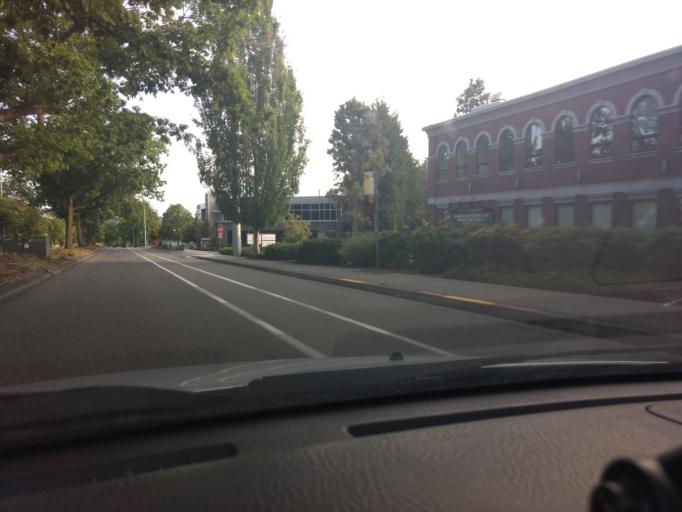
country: US
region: Washington
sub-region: King County
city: Kirkland
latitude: 47.6846
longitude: -122.2098
